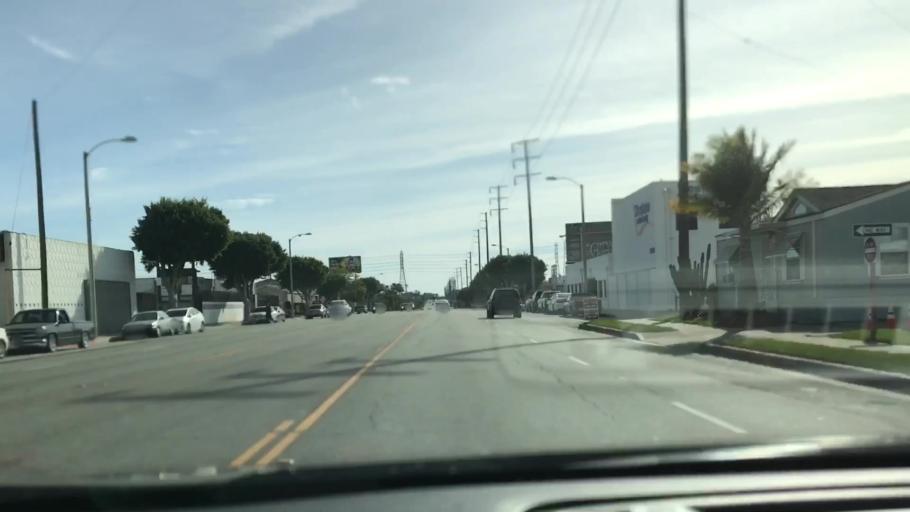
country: US
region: California
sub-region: Los Angeles County
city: Gardena
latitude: 33.8767
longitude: -118.3092
